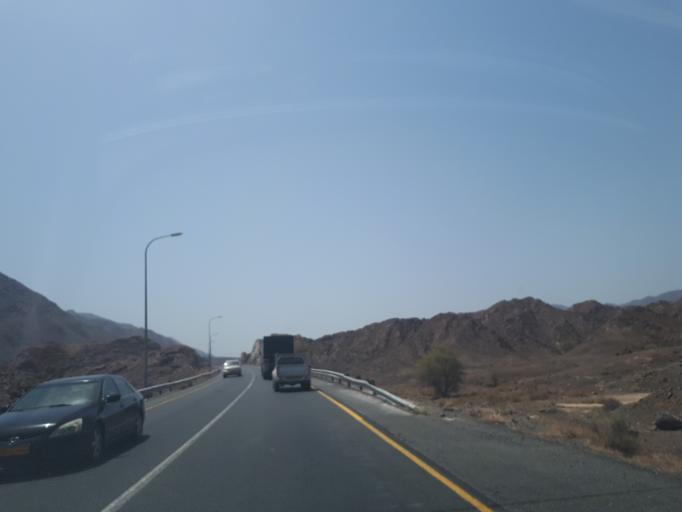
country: OM
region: Muhafazat ad Dakhiliyah
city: Sufalat Sama'il
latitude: 23.2115
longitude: 58.0779
